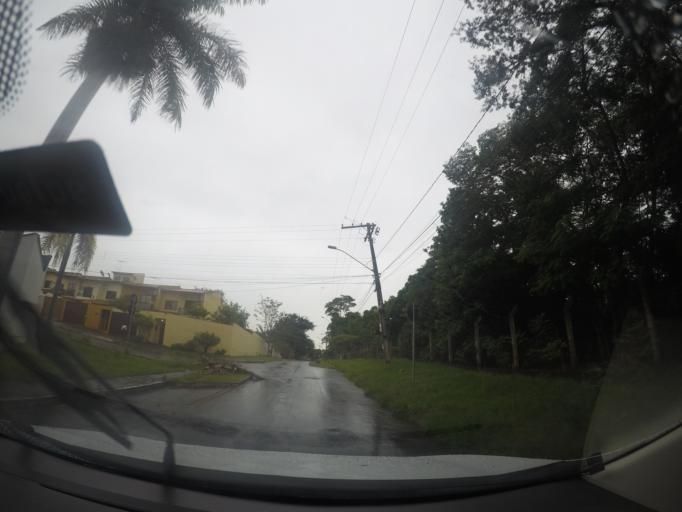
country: BR
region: Goias
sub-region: Goiania
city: Goiania
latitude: -16.6439
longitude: -49.2235
